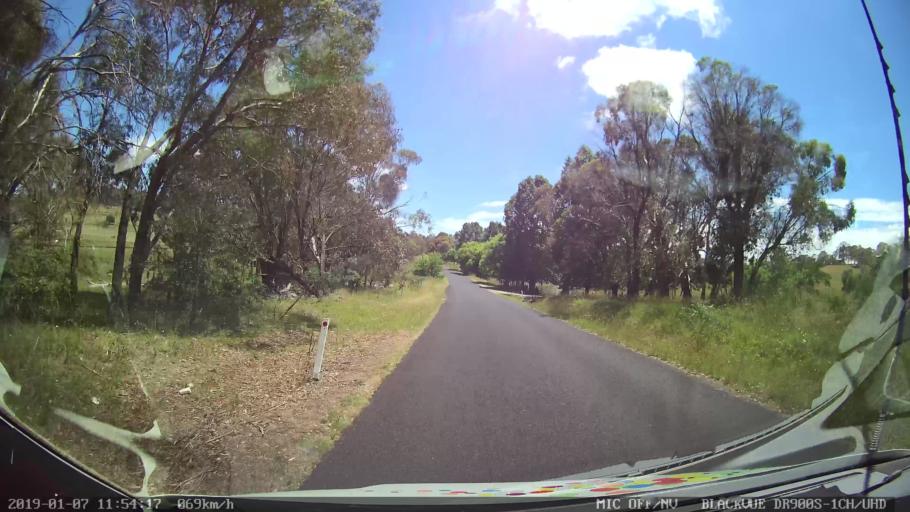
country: AU
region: New South Wales
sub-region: Guyra
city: Guyra
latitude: -30.2977
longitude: 151.6642
